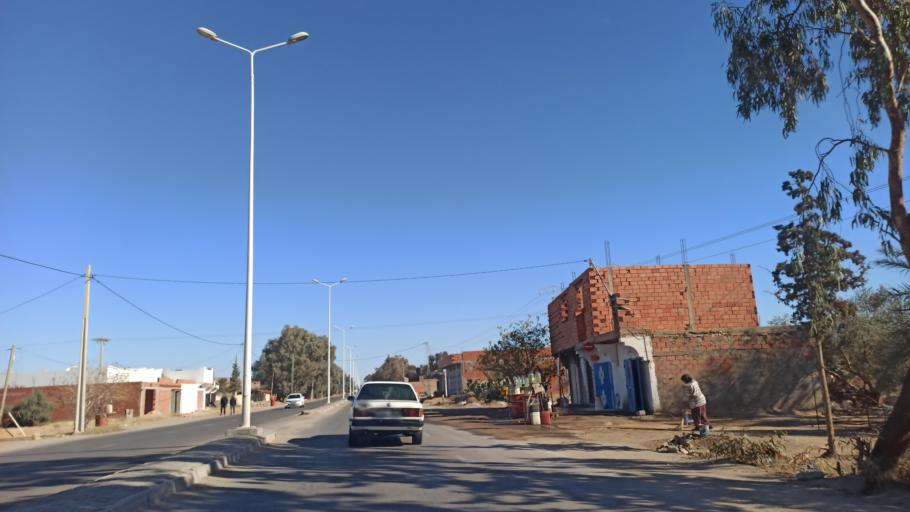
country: TN
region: Gafsa
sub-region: Gafsa Municipality
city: Gafsa
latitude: 34.4030
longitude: 8.7271
